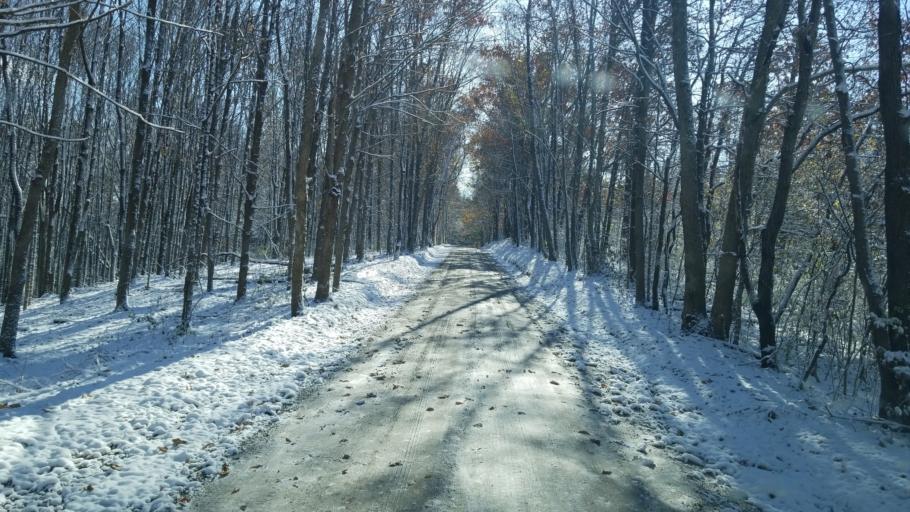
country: US
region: Ohio
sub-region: Licking County
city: Newark
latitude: 40.1497
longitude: -82.3493
